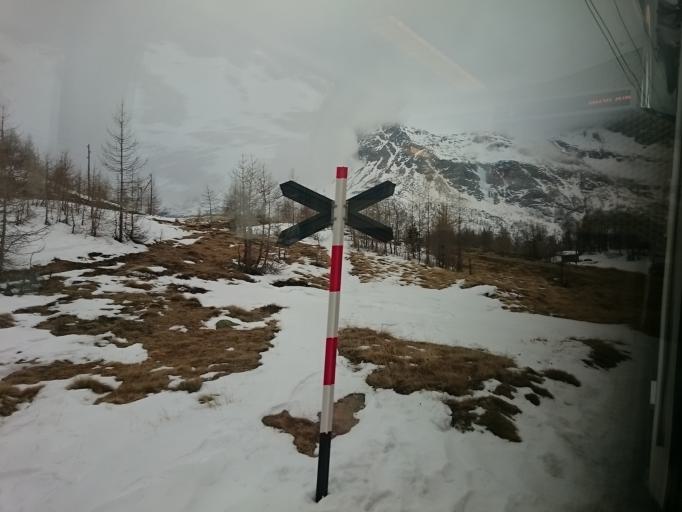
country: CH
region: Grisons
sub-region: Bernina District
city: Poschiavo
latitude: 46.3794
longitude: 10.0293
